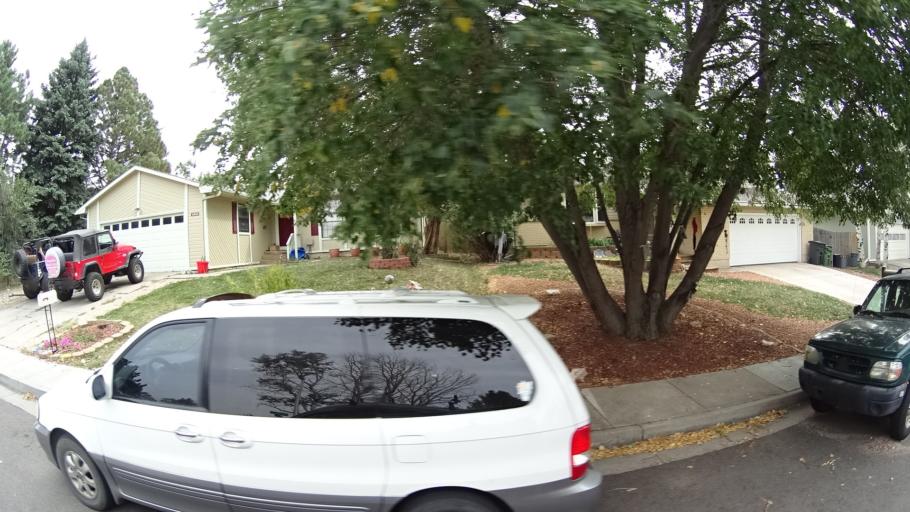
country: US
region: Colorado
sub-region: El Paso County
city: Cimarron Hills
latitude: 38.9001
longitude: -104.7358
